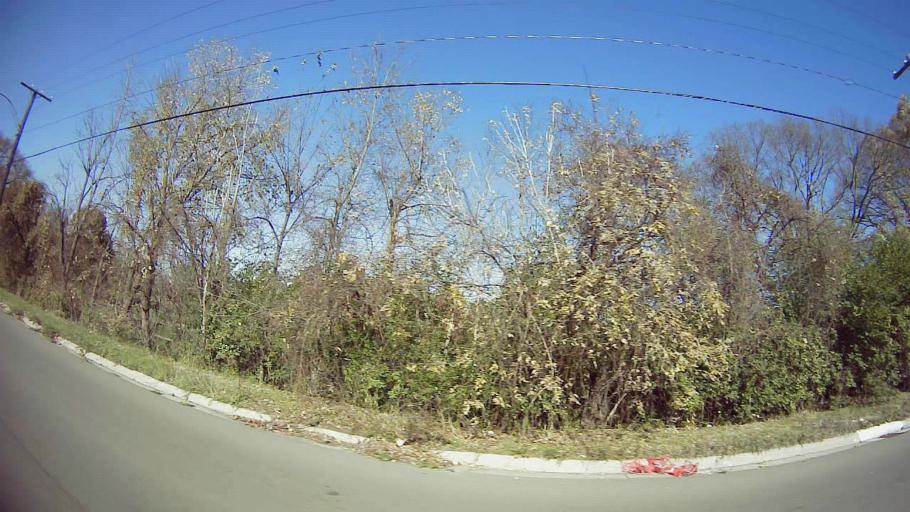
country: US
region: Michigan
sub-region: Wayne County
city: Dearborn Heights
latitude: 42.3718
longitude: -83.2532
